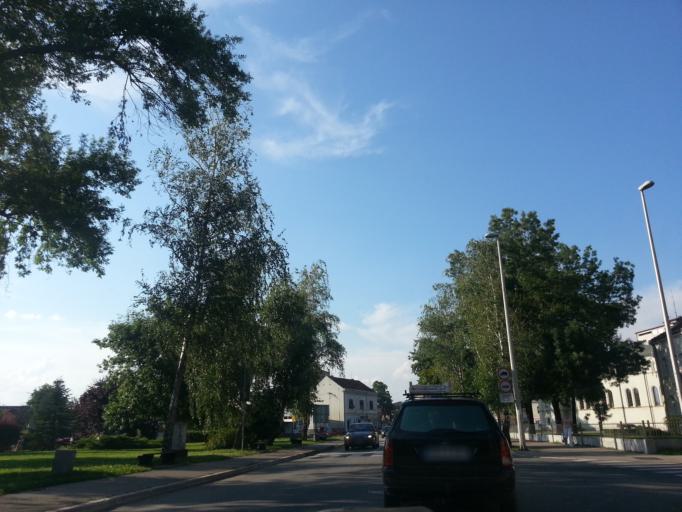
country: BA
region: Brcko
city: Brcko
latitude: 44.8717
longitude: 18.8100
